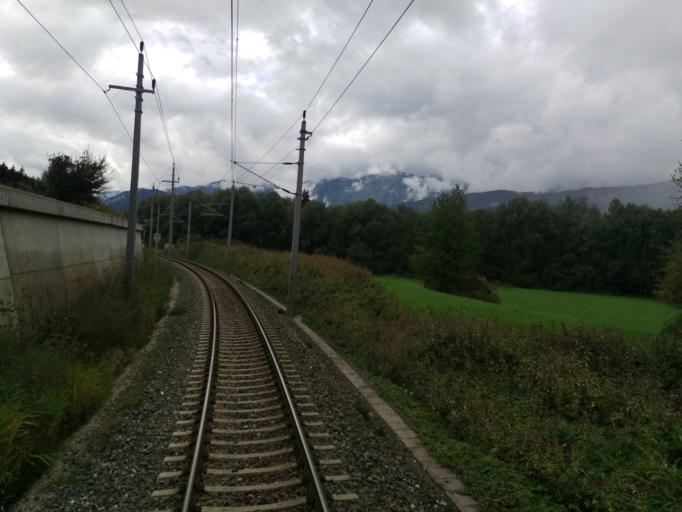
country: AT
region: Styria
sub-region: Politischer Bezirk Liezen
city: Lassing
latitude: 47.5496
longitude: 14.2698
